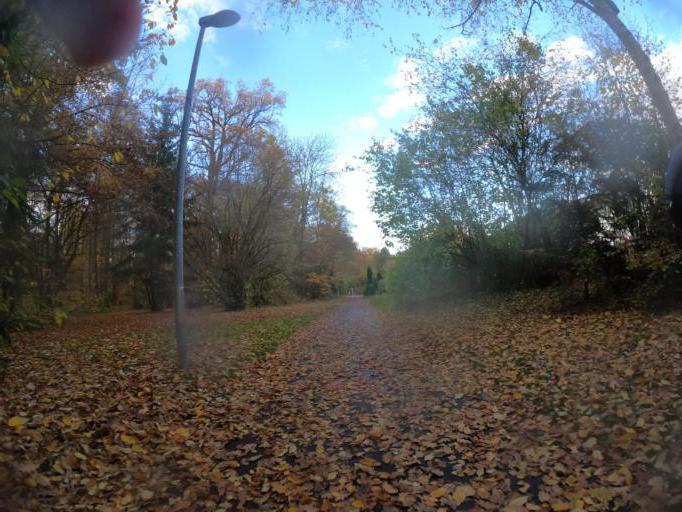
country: DE
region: Baden-Wuerttemberg
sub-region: Regierungsbezirk Stuttgart
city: Magstadt
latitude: 48.7304
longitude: 8.9983
